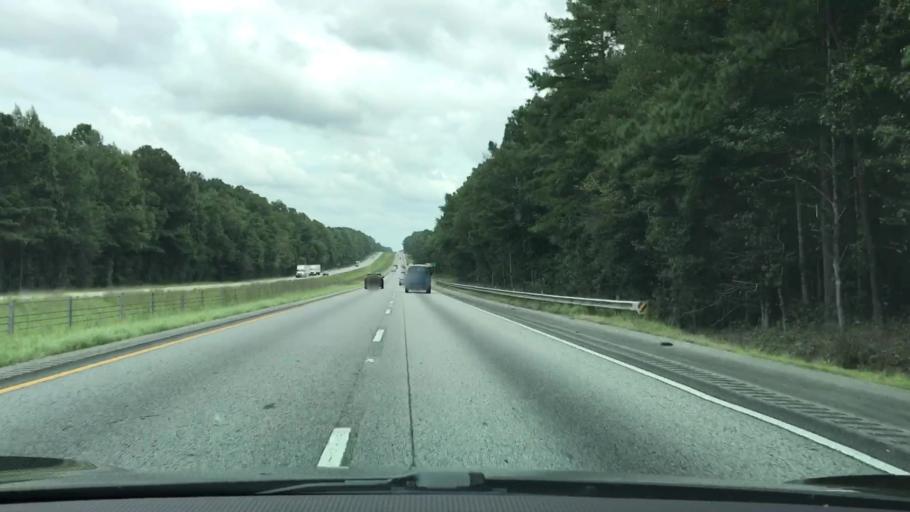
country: US
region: Alabama
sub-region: Chambers County
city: Huguley
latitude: 32.7551
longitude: -85.2730
